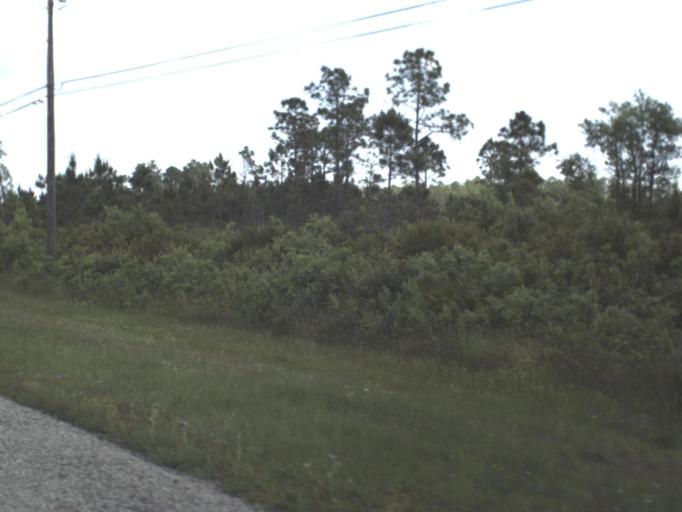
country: US
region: Florida
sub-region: Saint Johns County
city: Butler Beach
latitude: 29.7000
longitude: -81.2976
